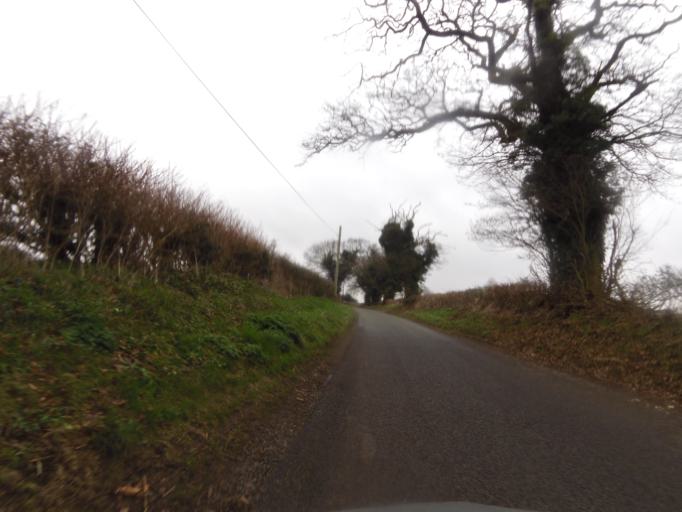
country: GB
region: England
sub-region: Norfolk
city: Briston
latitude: 52.8120
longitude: 1.0883
